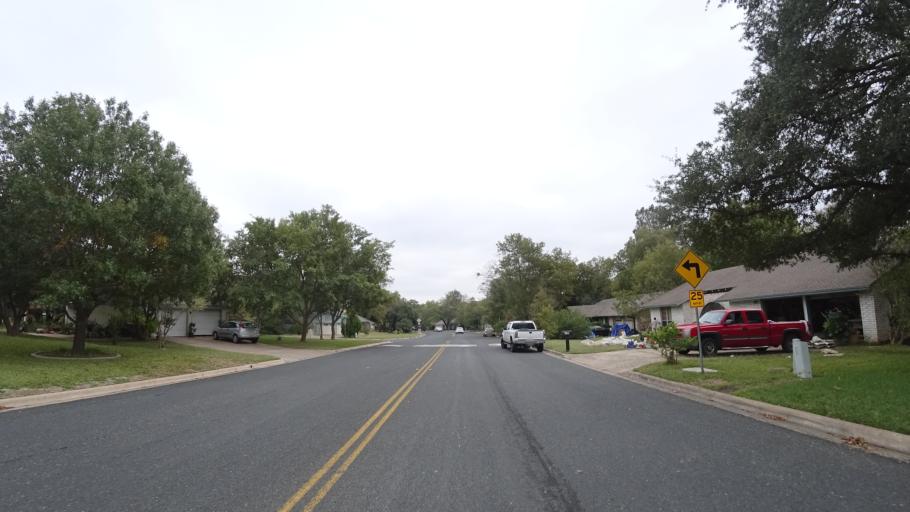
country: US
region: Texas
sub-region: Travis County
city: Barton Creek
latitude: 30.2375
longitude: -97.8868
